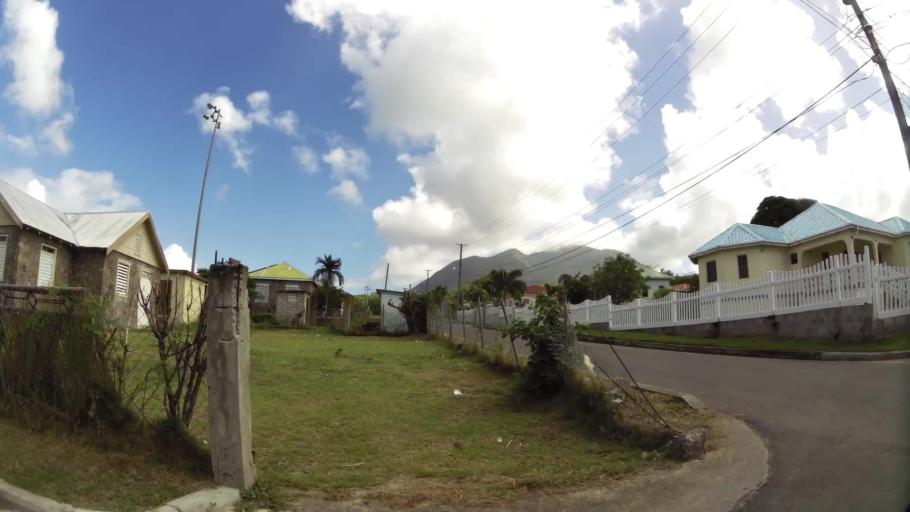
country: KN
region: Saint Thomas Lowland
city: Cotton Ground
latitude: 17.1733
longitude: -62.6193
